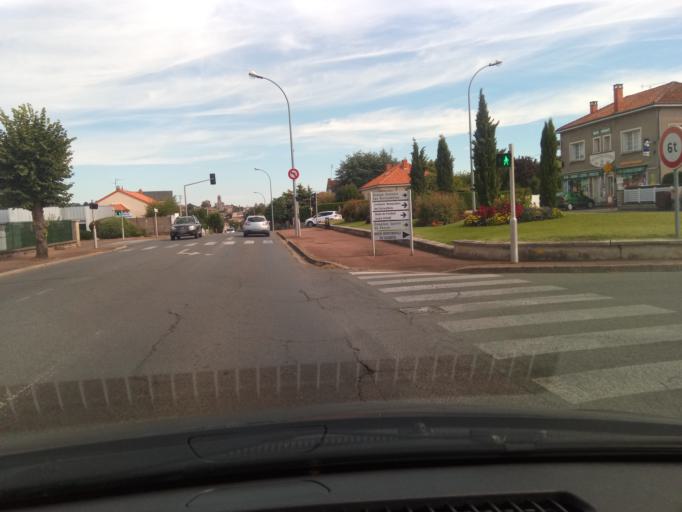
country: FR
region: Poitou-Charentes
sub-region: Departement de la Vienne
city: Chauvigny
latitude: 46.5684
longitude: 0.6329
